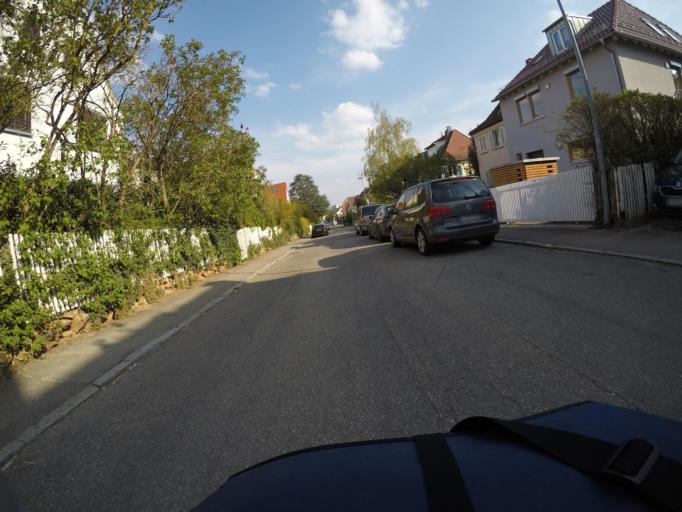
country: DE
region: Baden-Wuerttemberg
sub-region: Regierungsbezirk Stuttgart
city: Stuttgart-Ost
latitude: 48.7477
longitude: 9.2097
